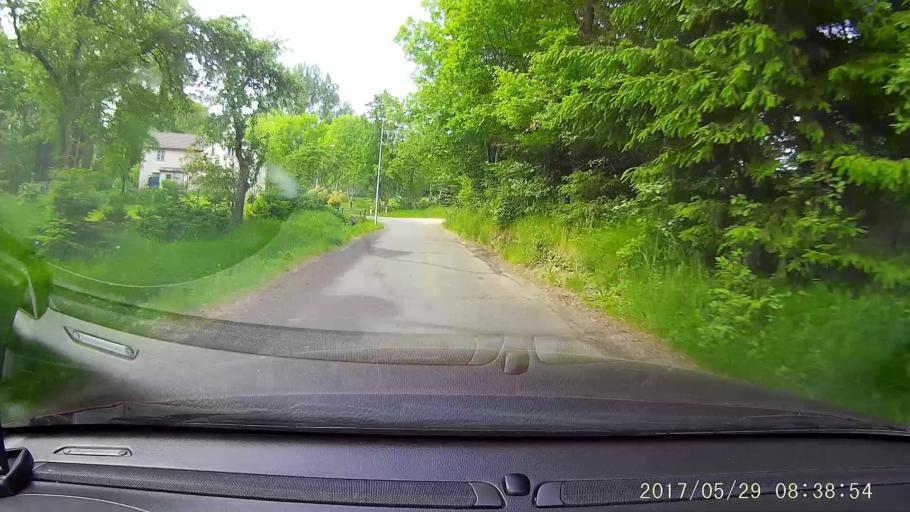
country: PL
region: Lower Silesian Voivodeship
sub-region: Powiat zlotoryjski
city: Swierzawa
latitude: 50.9876
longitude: 15.8358
